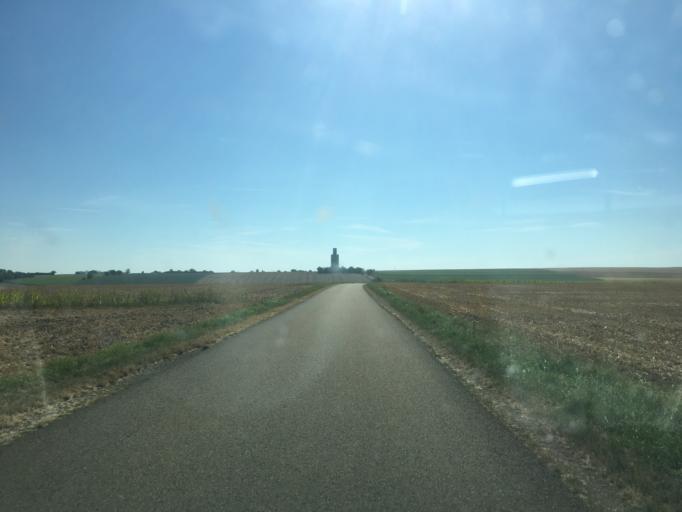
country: FR
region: Bourgogne
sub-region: Departement de l'Yonne
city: Fleury-la-Vallee
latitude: 47.9174
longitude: 3.4132
